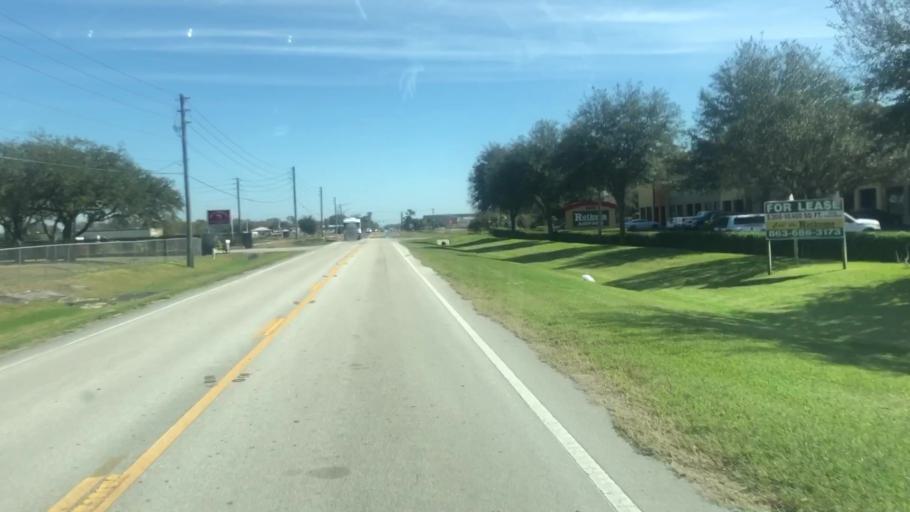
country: US
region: Florida
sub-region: Polk County
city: Winston
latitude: 27.9966
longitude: -82.0237
